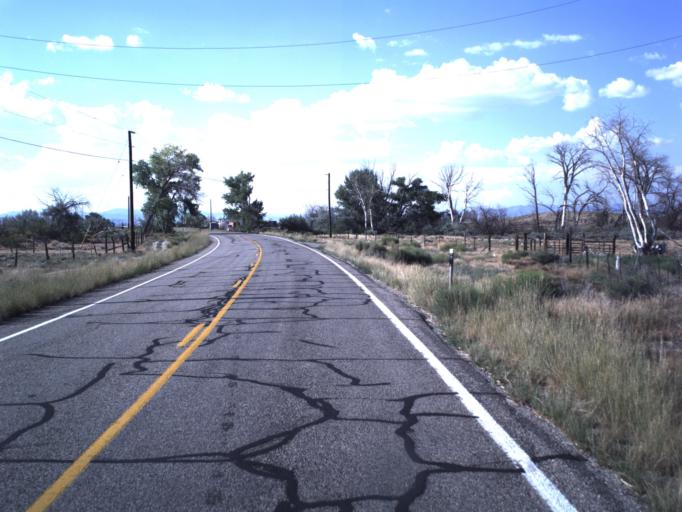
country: US
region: Utah
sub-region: Emery County
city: Huntington
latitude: 39.4069
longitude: -110.8526
